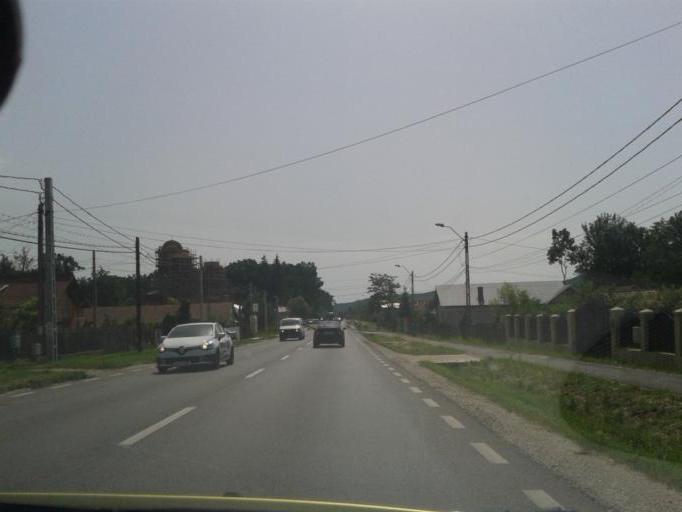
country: RO
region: Arges
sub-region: Comuna Bascov
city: Bascov
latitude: 44.8883
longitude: 24.7722
